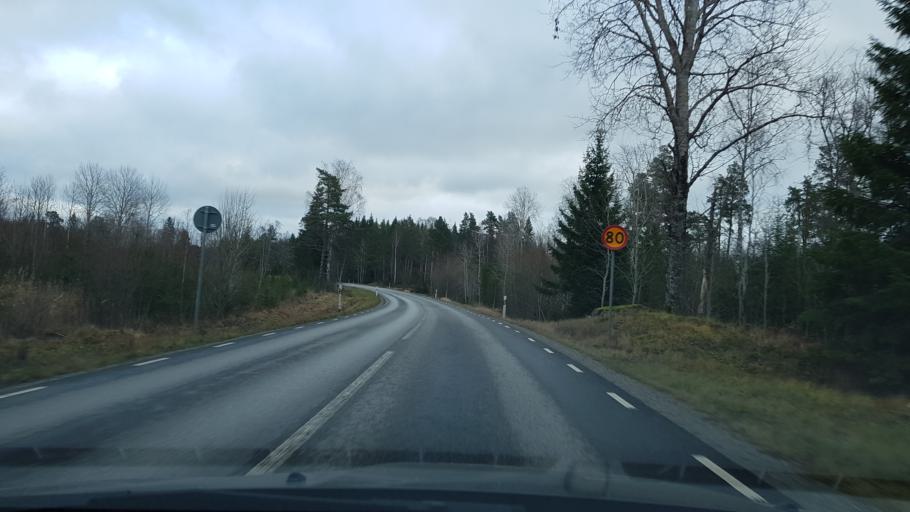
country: SE
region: Stockholm
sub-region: Norrtalje Kommun
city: Hallstavik
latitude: 60.0367
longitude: 18.5063
